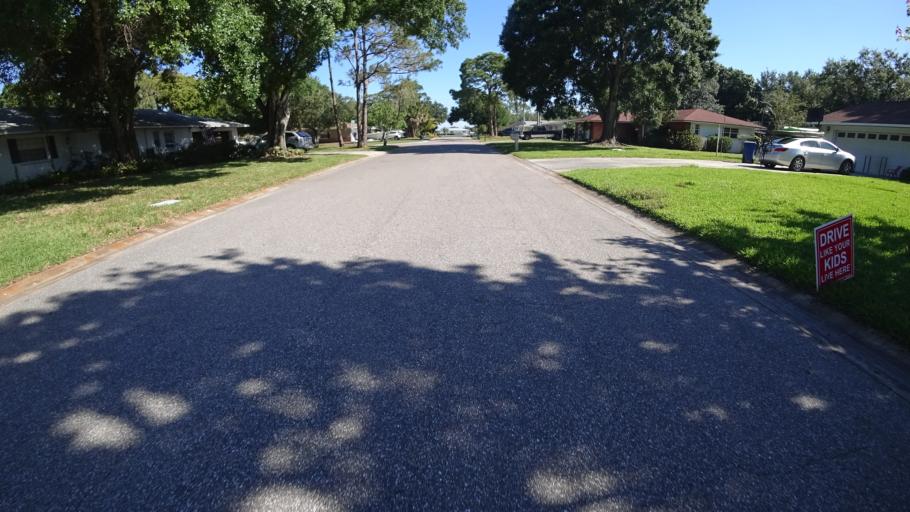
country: US
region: Florida
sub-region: Manatee County
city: West Bradenton
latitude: 27.4824
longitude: -82.6101
